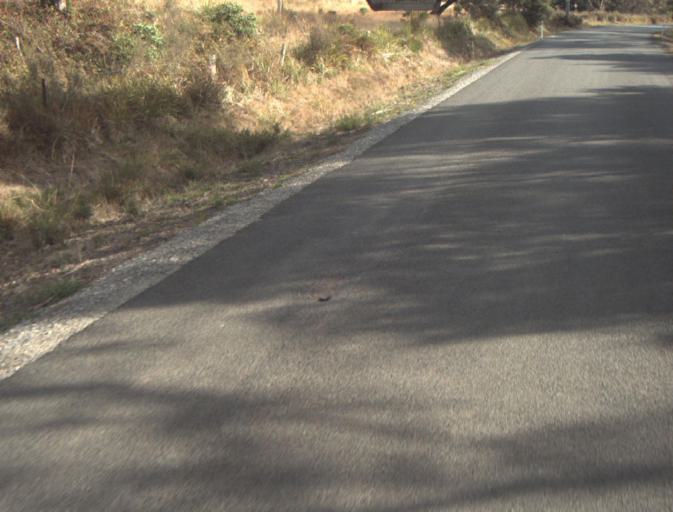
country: AU
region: Tasmania
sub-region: Launceston
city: Mayfield
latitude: -41.2381
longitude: 147.1799
